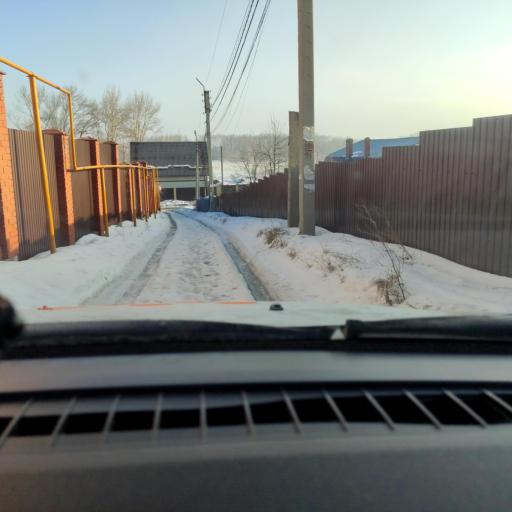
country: RU
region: Samara
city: Novokuybyshevsk
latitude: 53.1182
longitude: 49.9503
